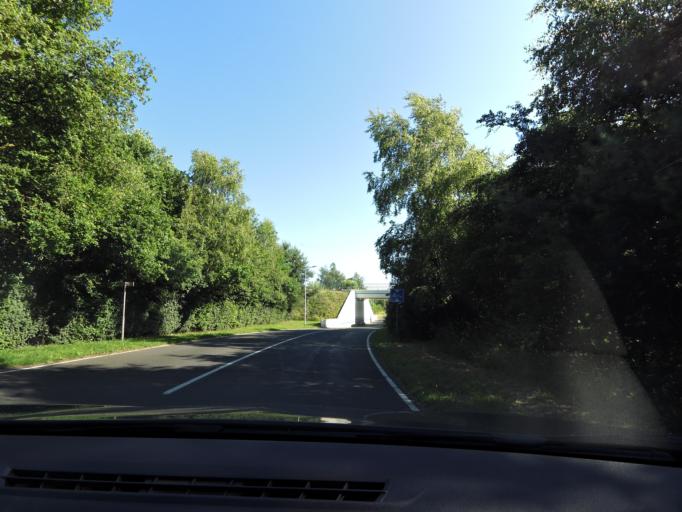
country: NL
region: Overijssel
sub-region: Gemeente Raalte
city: Raalte
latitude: 52.3700
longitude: 6.3992
